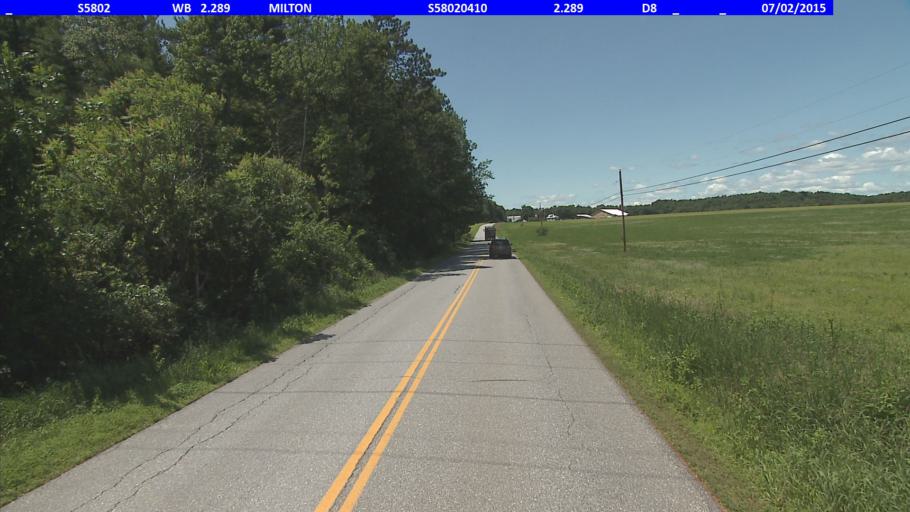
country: US
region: Vermont
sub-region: Chittenden County
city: Milton
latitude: 44.6314
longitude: -73.1816
